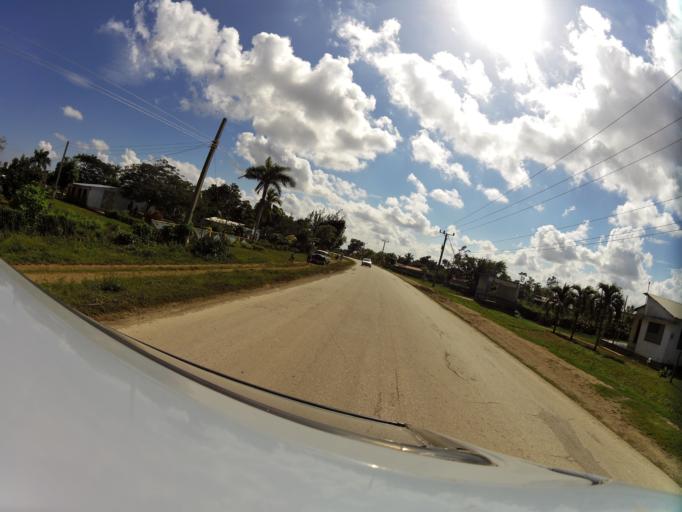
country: CU
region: Las Tunas
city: Jesus Menendez
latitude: 21.2260
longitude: -76.4245
